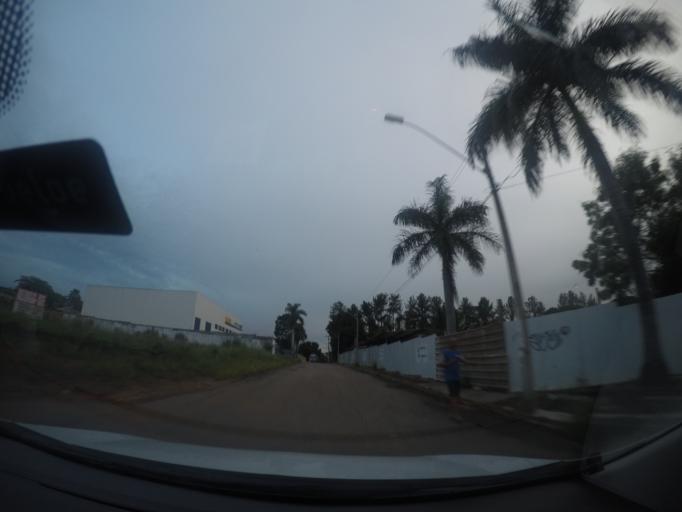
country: BR
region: Goias
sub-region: Goiania
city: Goiania
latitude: -16.6407
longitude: -49.2458
